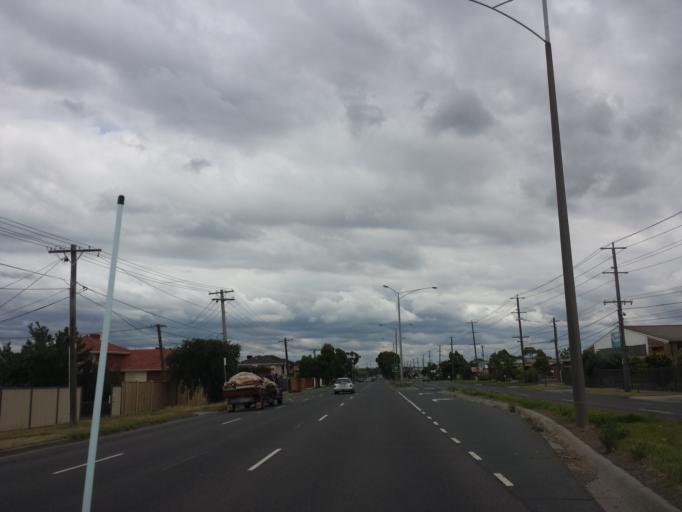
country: AU
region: Victoria
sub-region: Whittlesea
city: Thomastown
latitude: -37.6933
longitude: 144.9956
